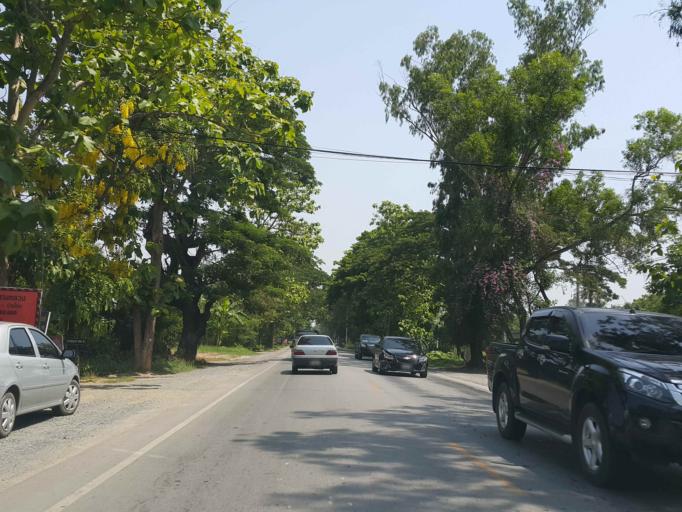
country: TH
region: Chiang Mai
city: San Sai
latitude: 18.9559
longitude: 98.9840
